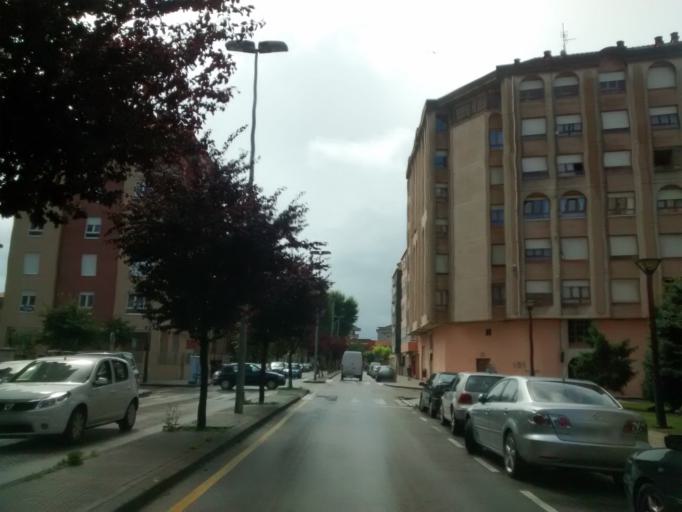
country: ES
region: Cantabria
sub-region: Provincia de Cantabria
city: Santona
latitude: 43.4429
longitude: -3.4528
